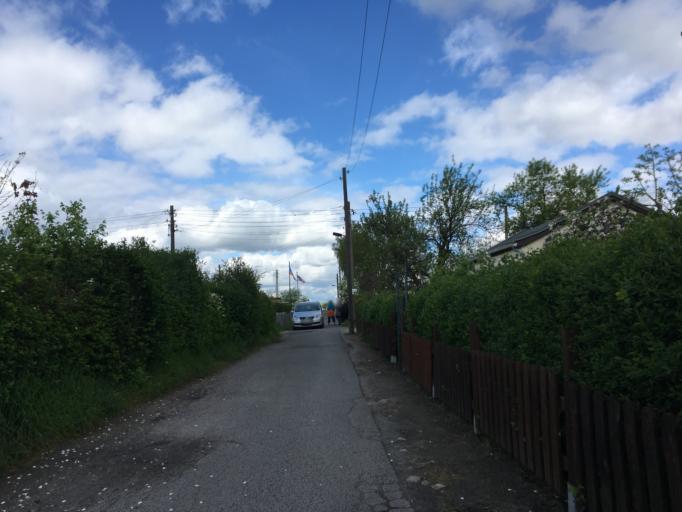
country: DE
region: Berlin
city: Buchholz
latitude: 52.6163
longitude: 13.4205
